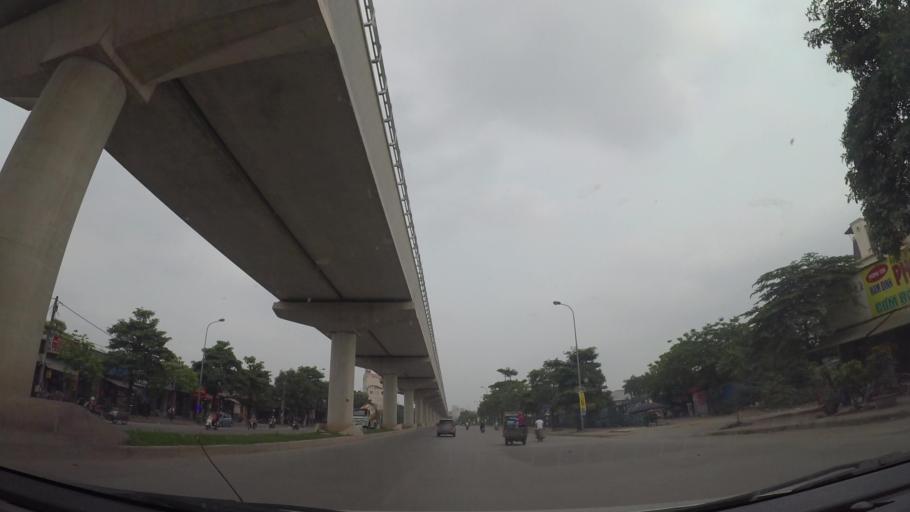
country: VN
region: Ha Noi
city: Cau Dien
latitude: 21.0504
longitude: 105.7385
